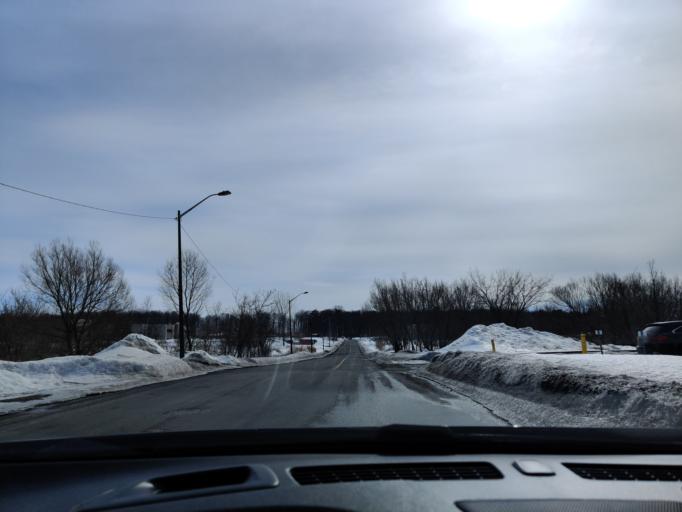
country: CA
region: Quebec
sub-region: Laurentides
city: Saint-Jerome
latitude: 45.7559
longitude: -73.9916
